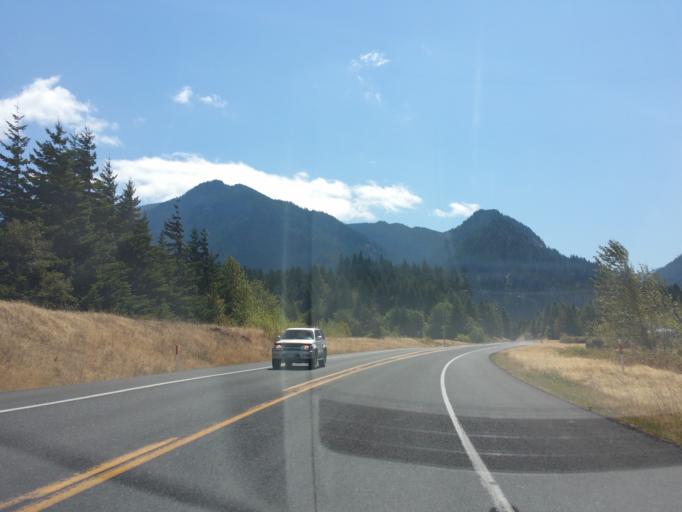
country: US
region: Oregon
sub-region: Hood River County
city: Cascade Locks
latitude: 45.6516
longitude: -121.9375
